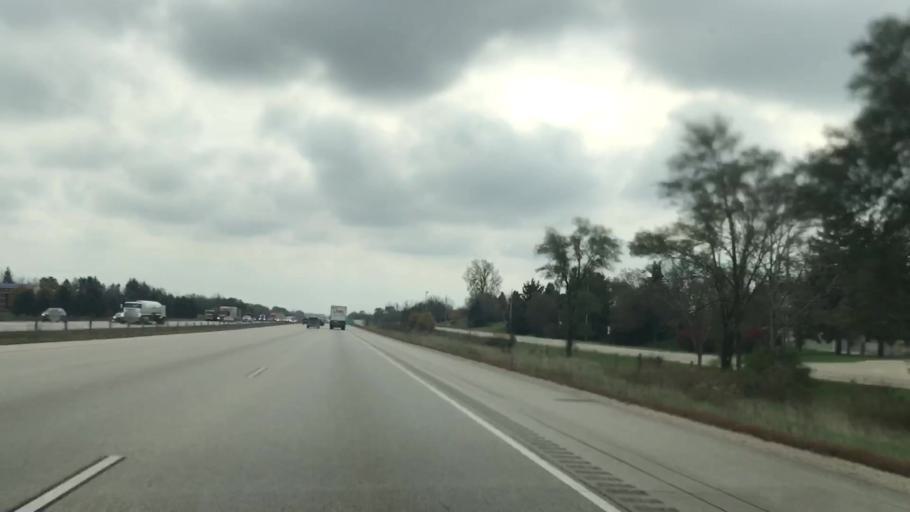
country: US
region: Wisconsin
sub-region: Washington County
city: Richfield
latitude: 43.2341
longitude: -88.1720
